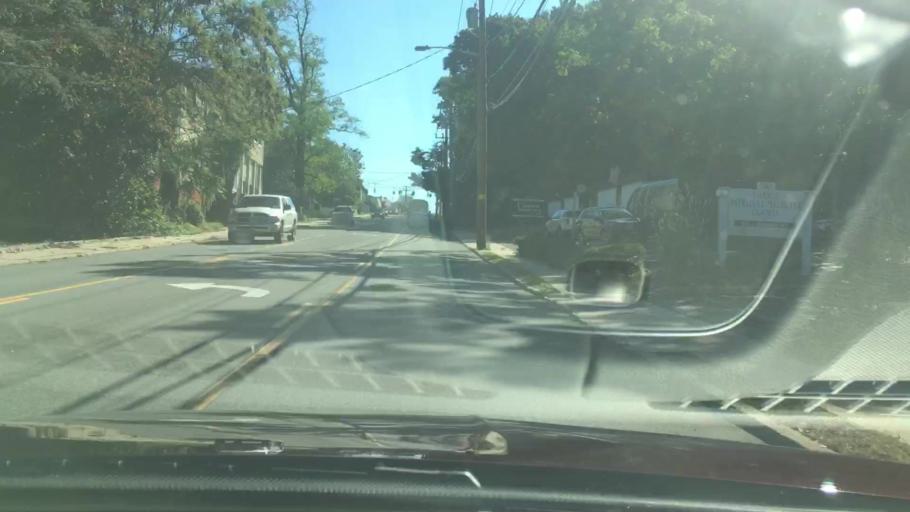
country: US
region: New York
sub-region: Suffolk County
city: Port Jefferson
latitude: 40.9376
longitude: -73.0584
